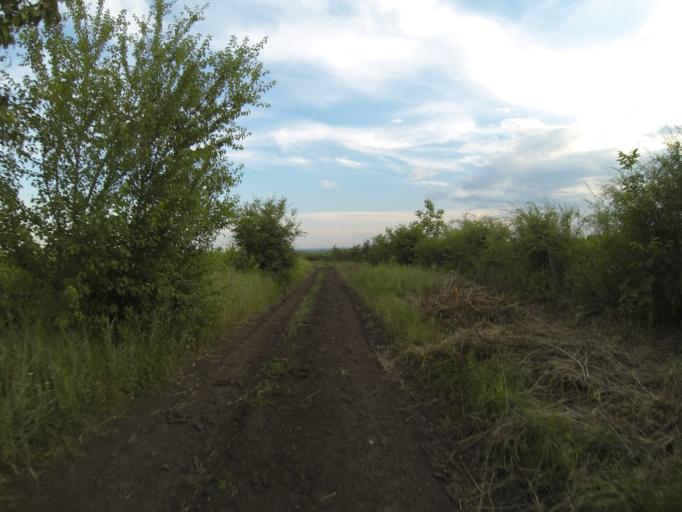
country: RO
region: Dolj
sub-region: Comuna Ceratu
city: Ceratu
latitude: 44.1117
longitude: 23.6818
